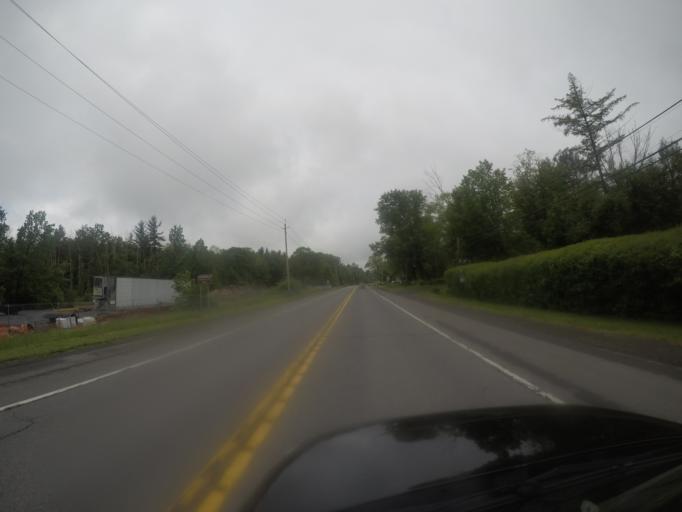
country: US
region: New York
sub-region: Ulster County
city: Shokan
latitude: 41.9754
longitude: -74.1973
